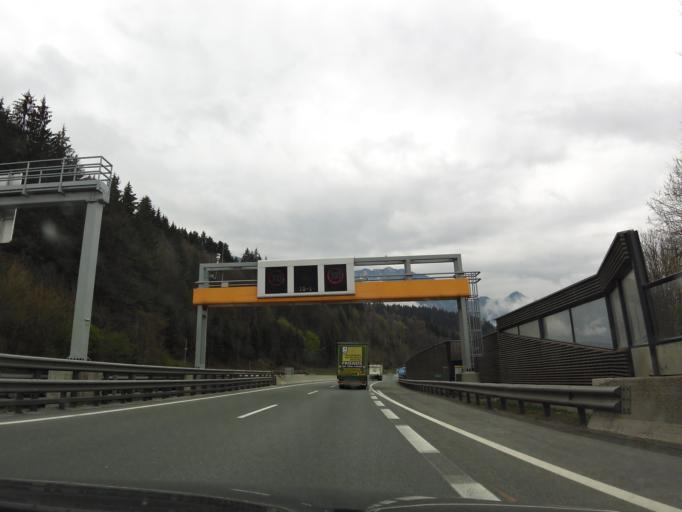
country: AT
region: Tyrol
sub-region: Politischer Bezirk Kufstein
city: Angath
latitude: 47.5008
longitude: 12.0582
